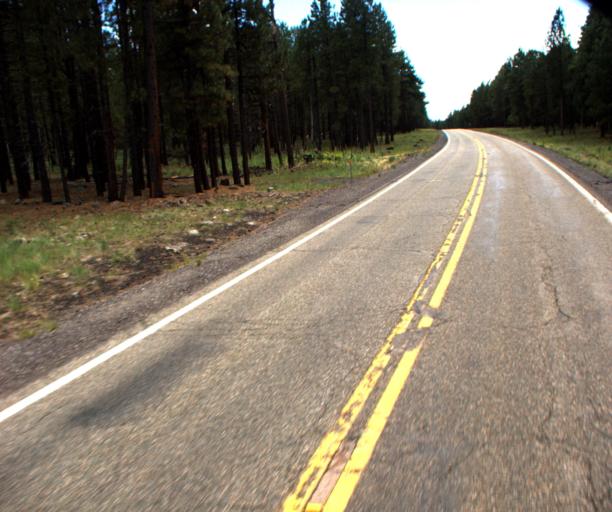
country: US
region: Arizona
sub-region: Coconino County
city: Flagstaff
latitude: 35.3192
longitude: -111.7749
